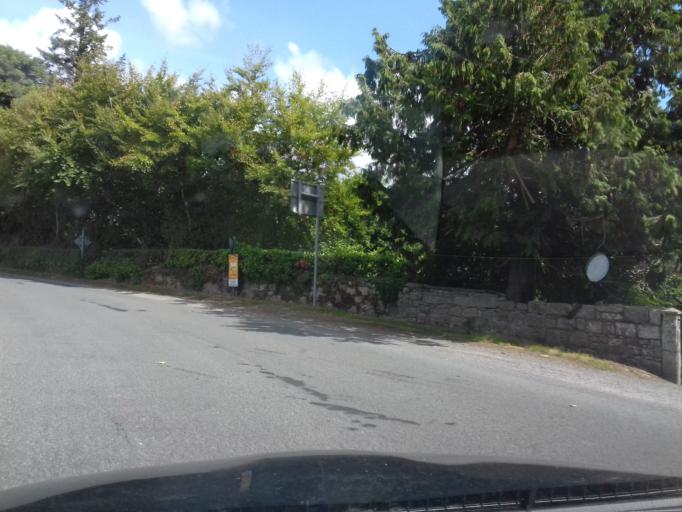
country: IE
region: Leinster
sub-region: Kilkenny
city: Graiguenamanagh
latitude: 52.5970
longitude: -6.9162
